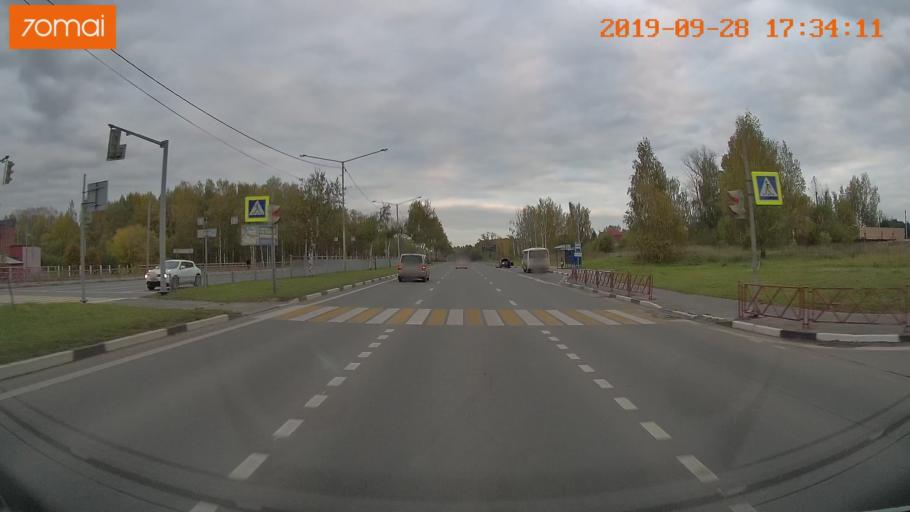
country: RU
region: Jaroslavl
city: Yaroslavl
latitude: 57.5613
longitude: 39.9347
